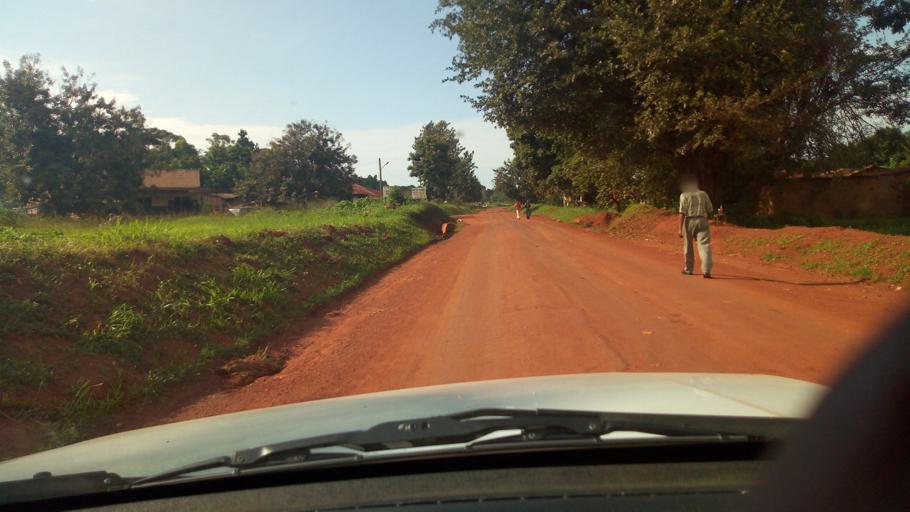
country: UG
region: Western Region
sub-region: Masindi District
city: Masindi
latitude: 1.6676
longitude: 31.7055
